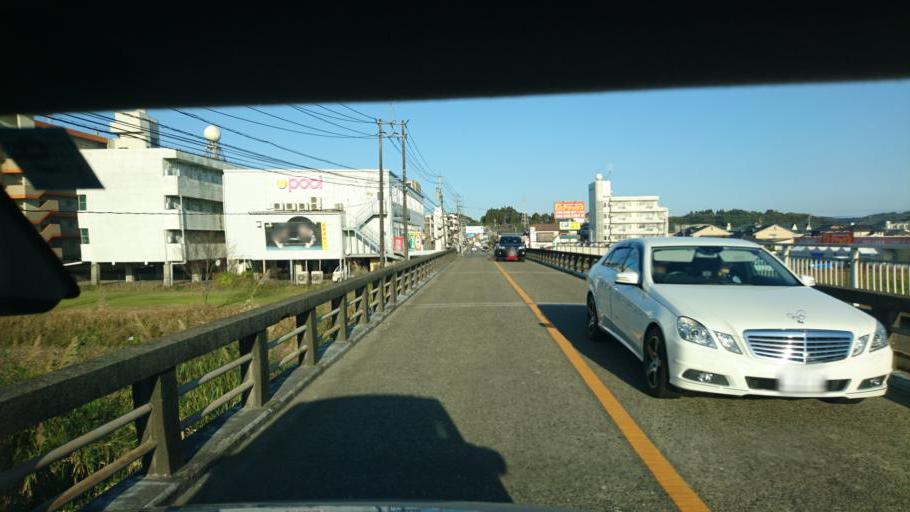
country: JP
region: Miyazaki
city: Miyazaki-shi
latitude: 31.8474
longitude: 131.3909
